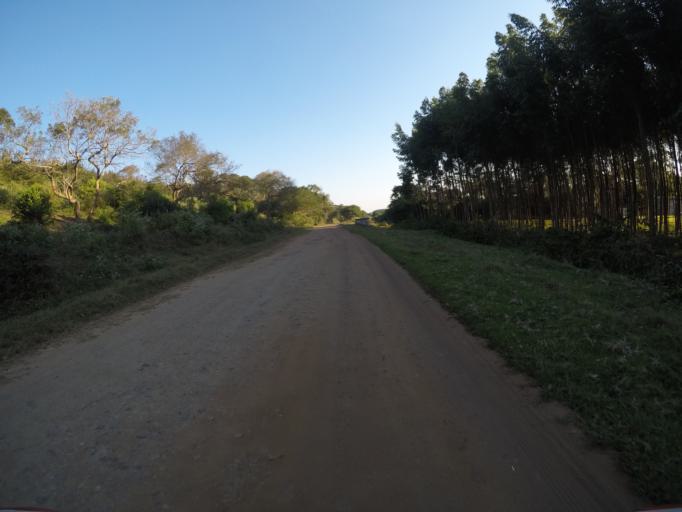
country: ZA
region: KwaZulu-Natal
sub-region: uThungulu District Municipality
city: KwaMbonambi
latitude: -28.7026
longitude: 32.1901
